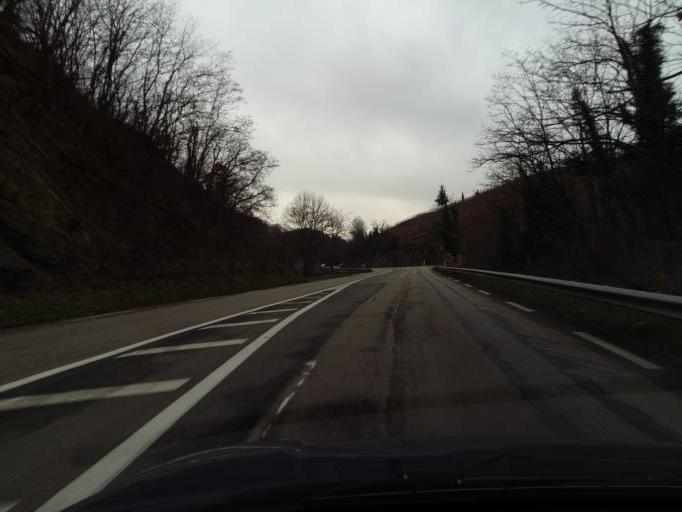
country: FR
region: Rhone-Alpes
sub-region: Departement de l'Ardeche
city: Andance
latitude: 45.2533
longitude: 4.7681
